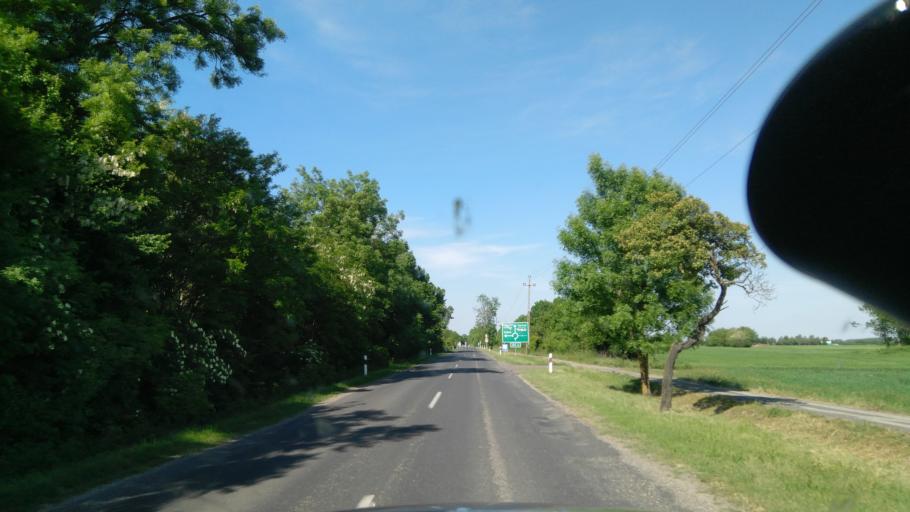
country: HU
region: Bekes
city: Sarkad
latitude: 46.7147
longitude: 21.3286
